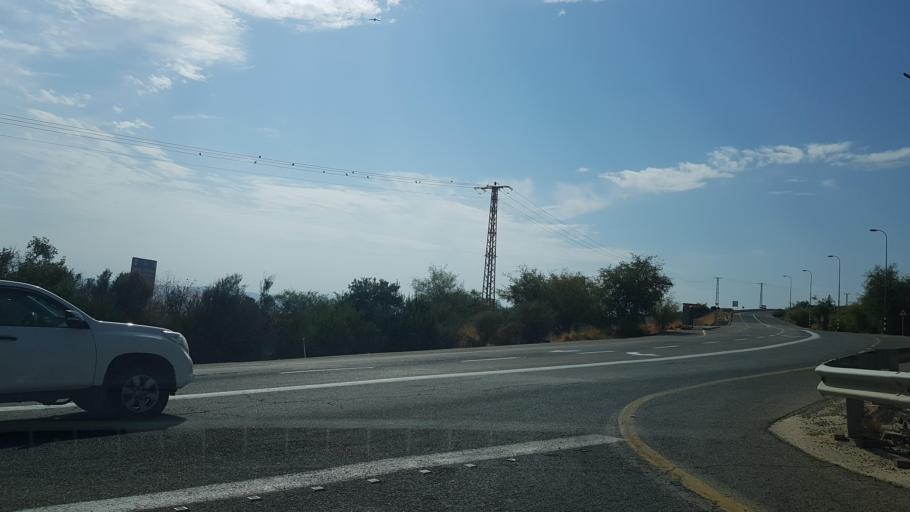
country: SY
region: Quneitra
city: Al Butayhah
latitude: 32.9126
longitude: 35.5966
